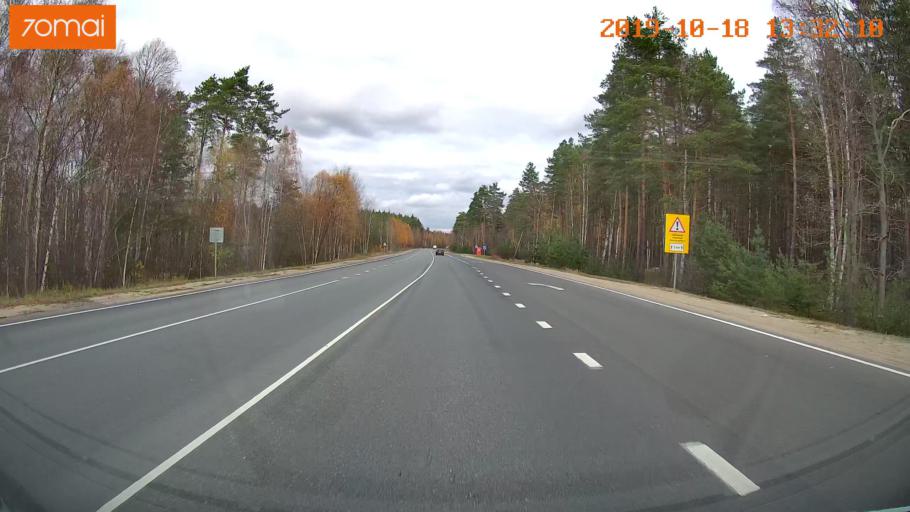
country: RU
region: Rjazan
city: Solotcha
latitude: 54.8294
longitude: 39.9149
